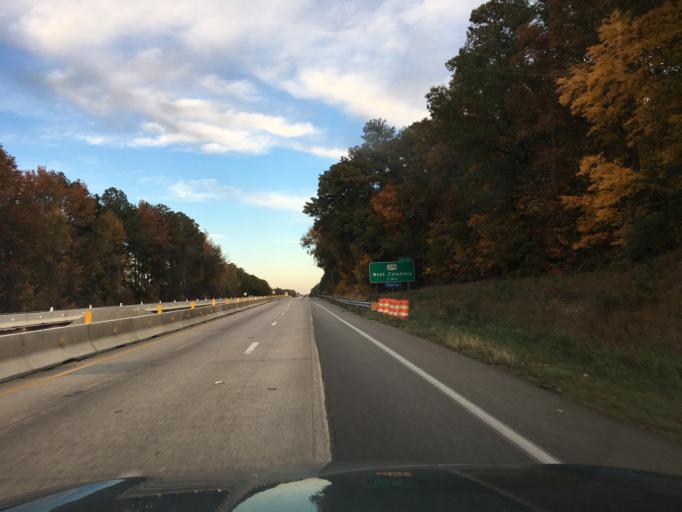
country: US
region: South Carolina
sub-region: Lexington County
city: Oak Grove
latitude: 34.0035
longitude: -81.1676
